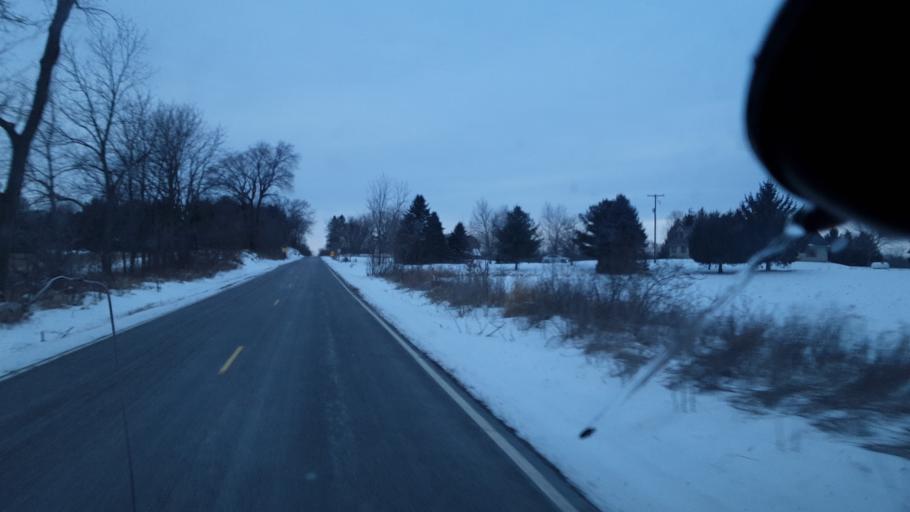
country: US
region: Michigan
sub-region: Ingham County
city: Leslie
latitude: 42.4464
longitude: -84.3405
